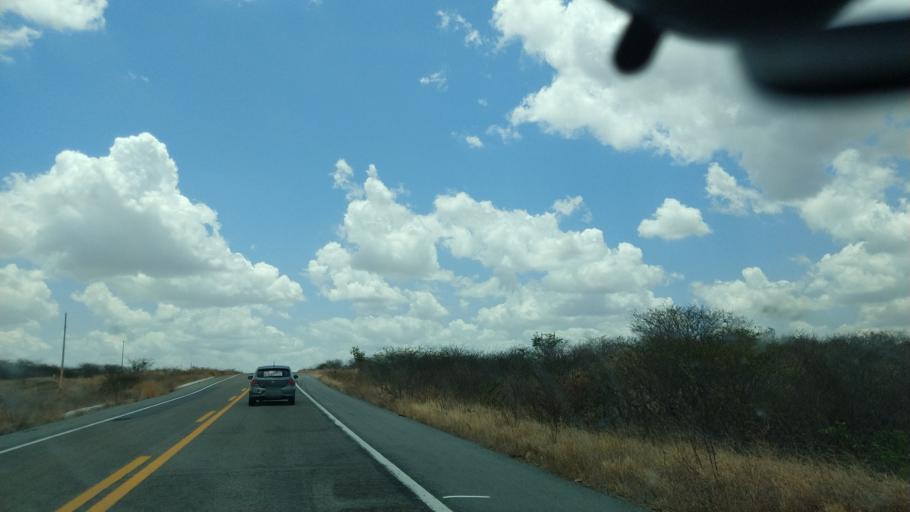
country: BR
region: Rio Grande do Norte
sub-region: Cerro Cora
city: Cerro Cora
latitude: -6.2033
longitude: -36.3291
